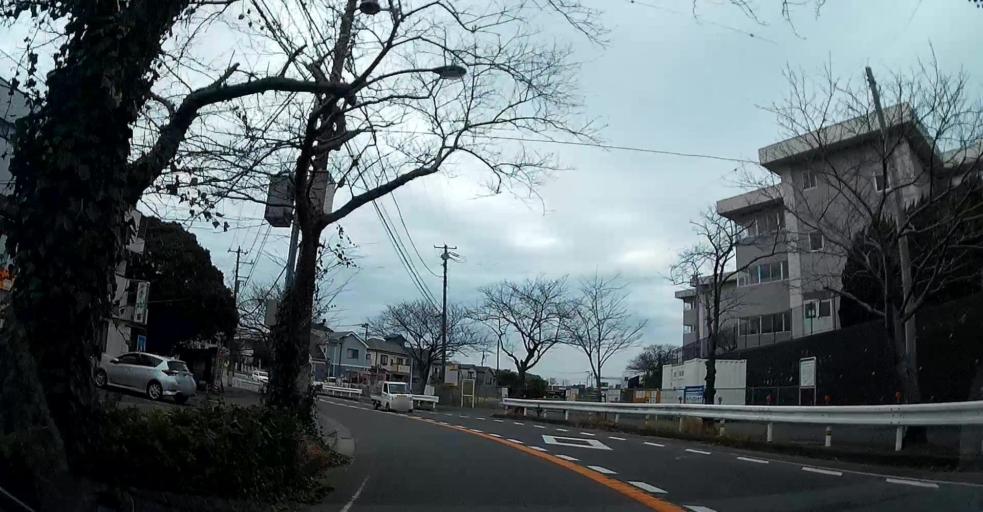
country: JP
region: Kanagawa
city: Yokosuka
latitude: 35.2138
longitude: 139.6759
